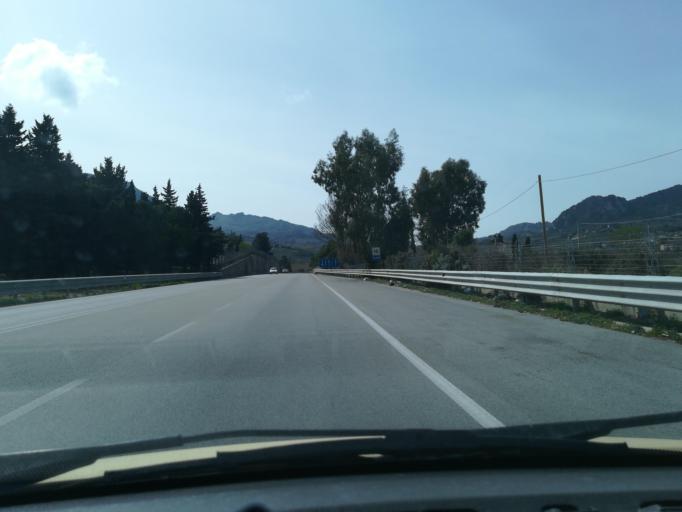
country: IT
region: Sicily
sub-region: Palermo
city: Cannizzaro-Favara
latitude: 38.0364
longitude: 13.2670
